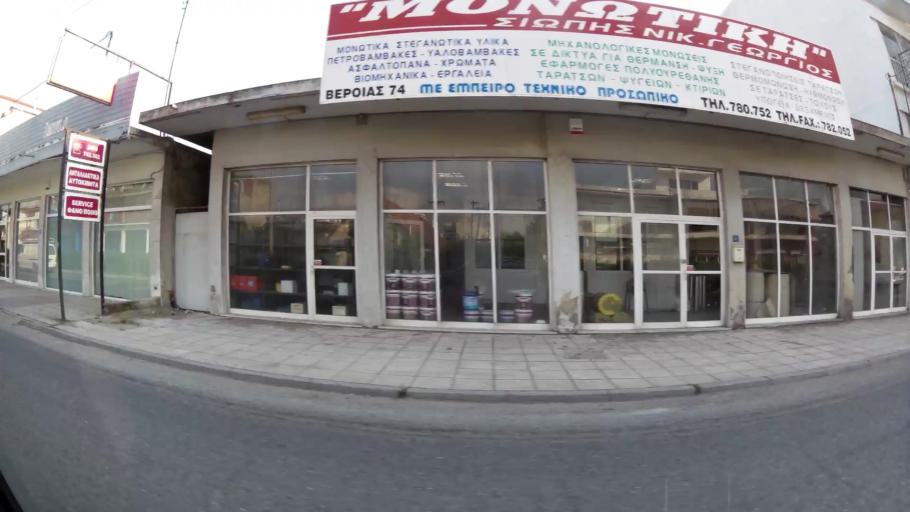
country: GR
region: Central Macedonia
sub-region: Nomos Thessalonikis
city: Diavata
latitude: 40.6835
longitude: 22.8600
